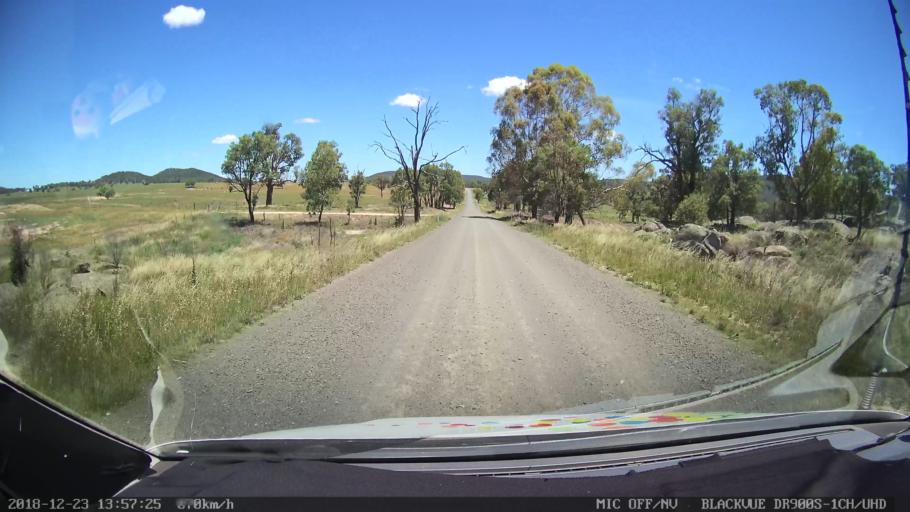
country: AU
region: New South Wales
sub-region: Tamworth Municipality
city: Manilla
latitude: -30.5877
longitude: 151.0938
